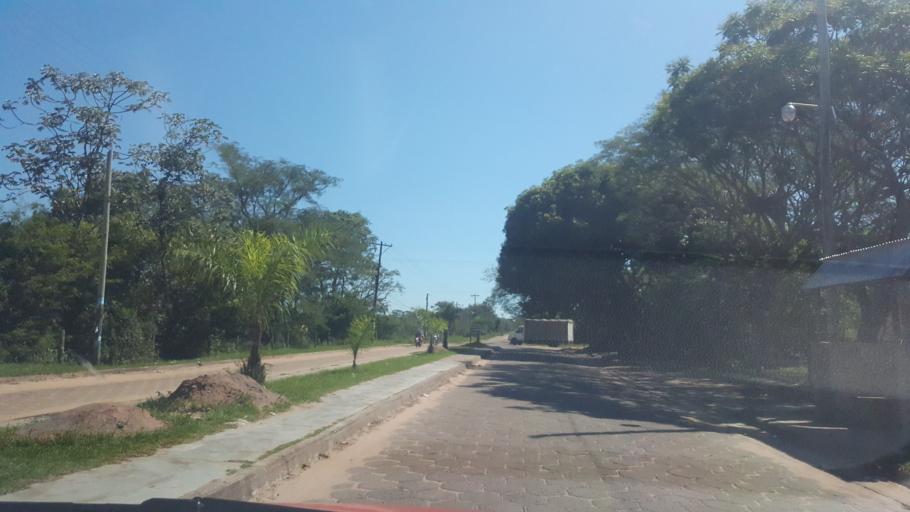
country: AR
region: Corrientes
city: Ituzaingo
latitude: -27.5954
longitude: -56.7051
